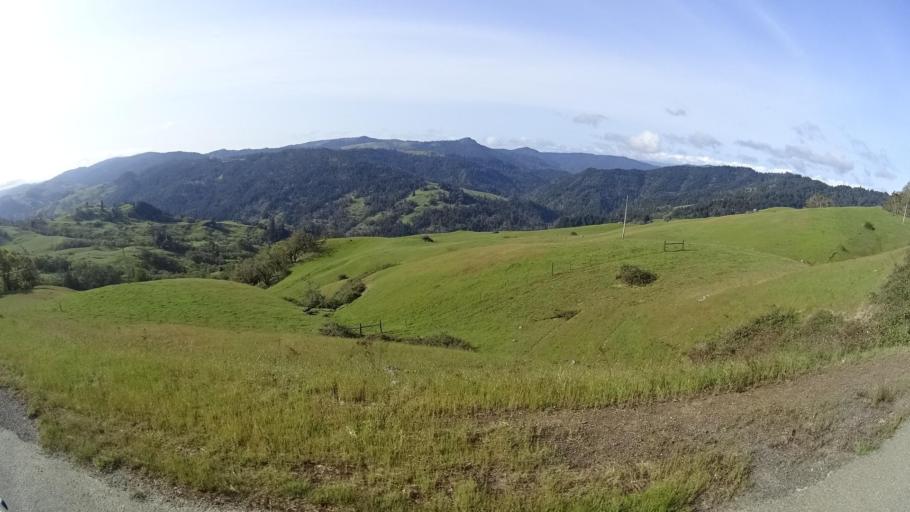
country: US
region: California
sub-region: Humboldt County
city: Hydesville
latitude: 40.6385
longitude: -123.8957
